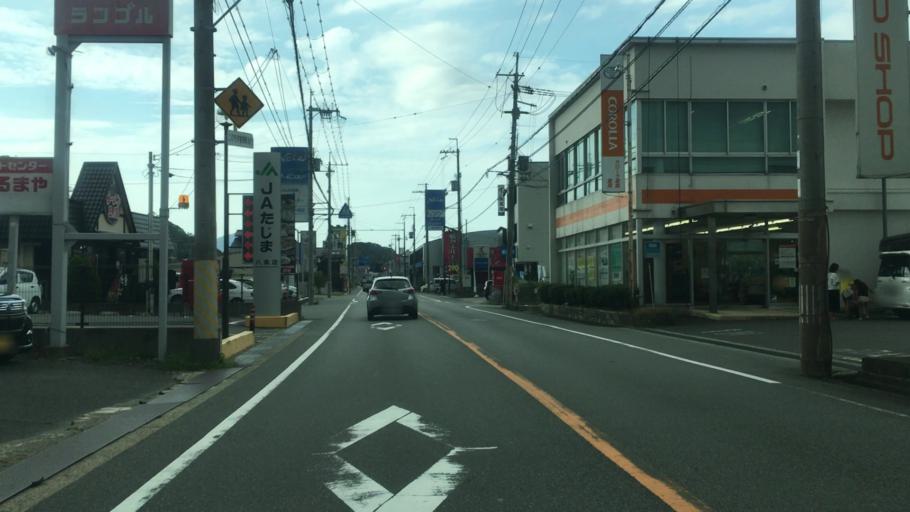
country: JP
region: Hyogo
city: Toyooka
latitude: 35.5255
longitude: 134.8212
